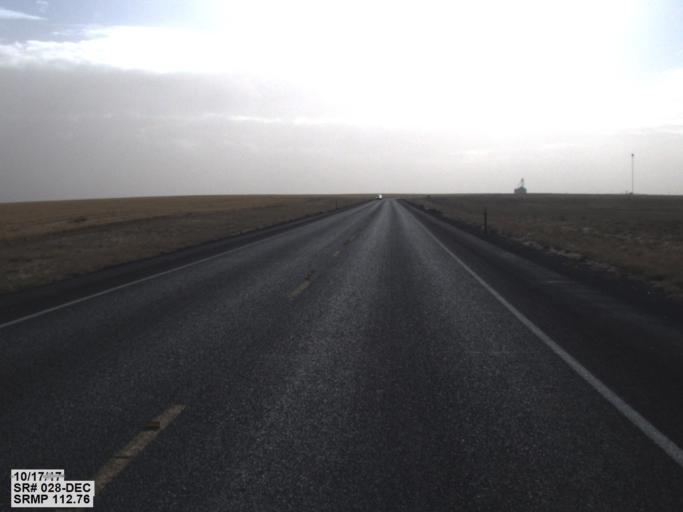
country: US
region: Washington
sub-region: Lincoln County
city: Davenport
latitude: 47.4340
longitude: -118.3355
